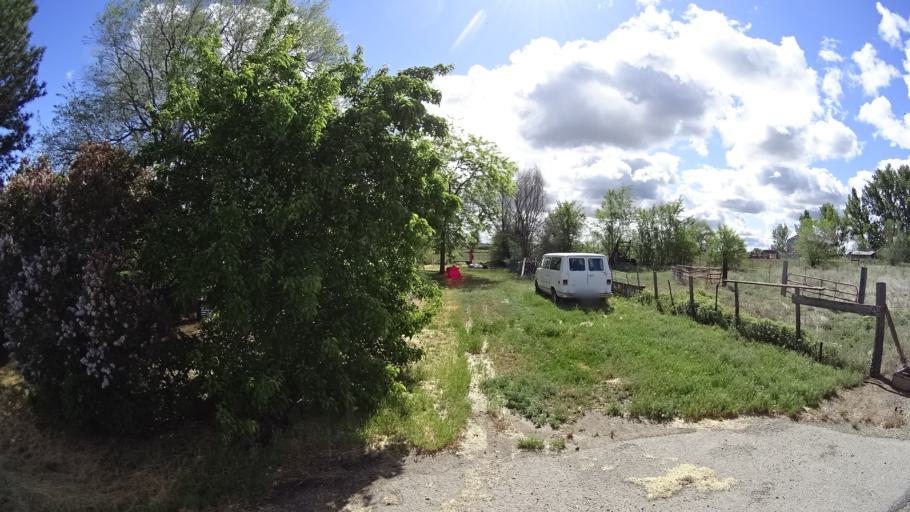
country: US
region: Idaho
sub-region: Ada County
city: Kuna
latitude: 43.5134
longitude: -116.4736
